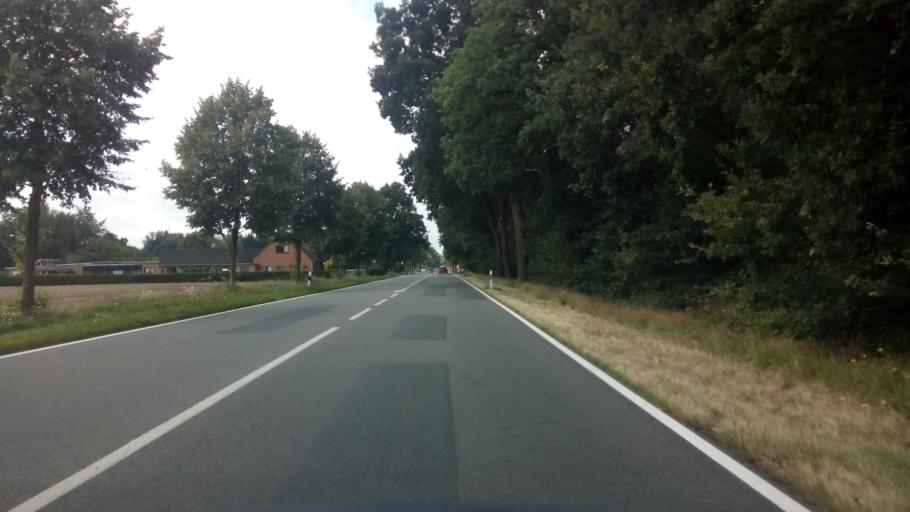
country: DE
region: Lower Saxony
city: Barnstorf
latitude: 52.7199
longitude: 8.5309
